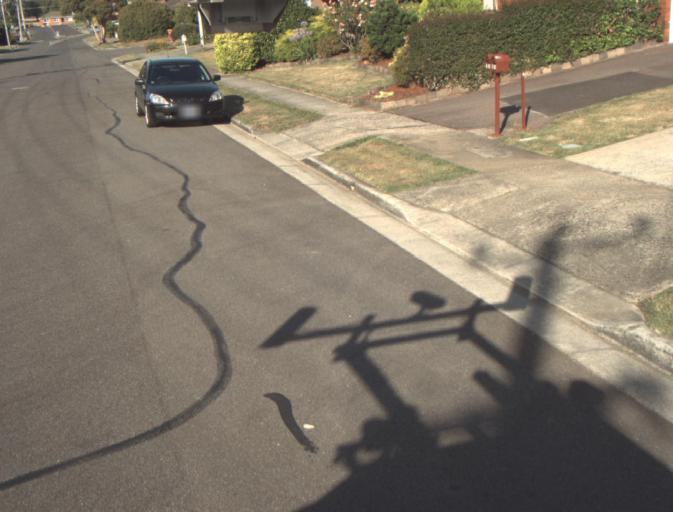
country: AU
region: Tasmania
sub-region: Launceston
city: Newnham
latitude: -41.3957
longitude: 147.1309
